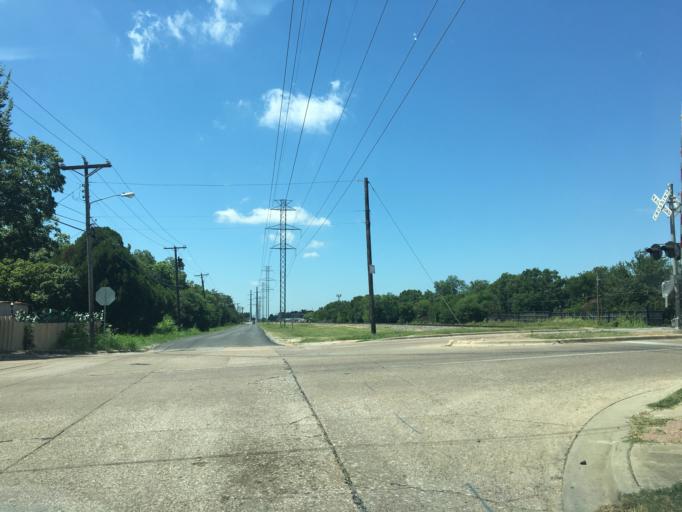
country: US
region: Texas
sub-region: Dallas County
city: Garland
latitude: 32.8403
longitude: -96.6864
